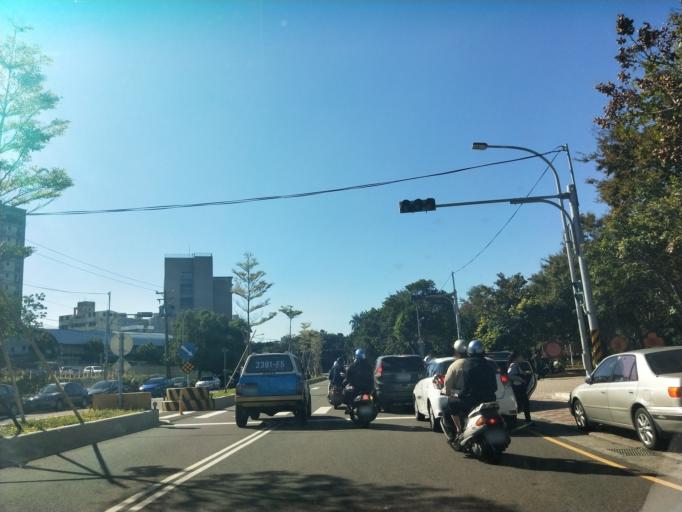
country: TW
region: Taiwan
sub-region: Hsinchu
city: Hsinchu
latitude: 24.7978
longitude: 121.0028
